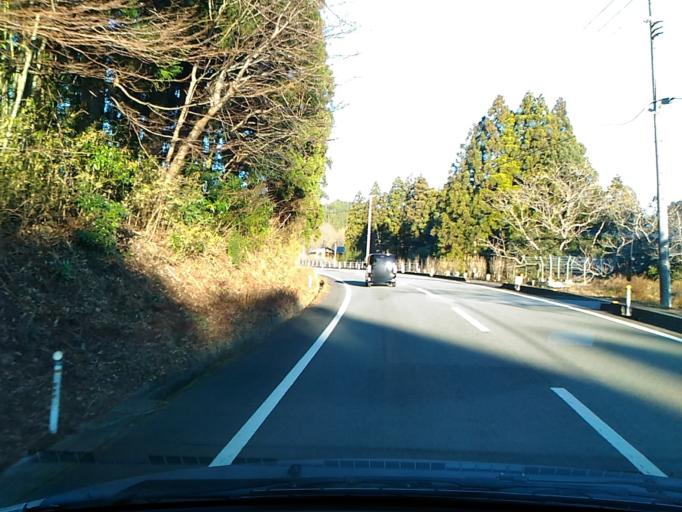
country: JP
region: Ibaraki
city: Kitaibaraki
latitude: 36.9288
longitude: 140.6937
